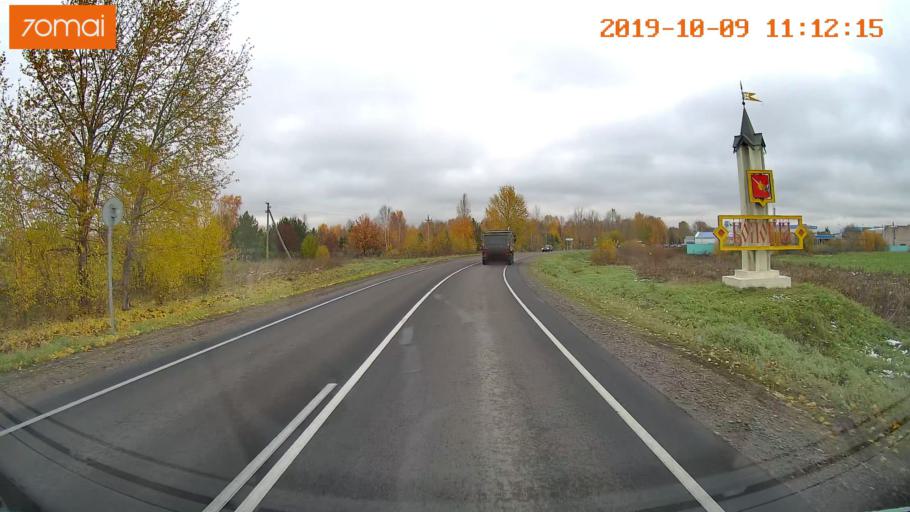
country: RU
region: Vologda
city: Vologda
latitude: 59.1760
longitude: 39.8283
